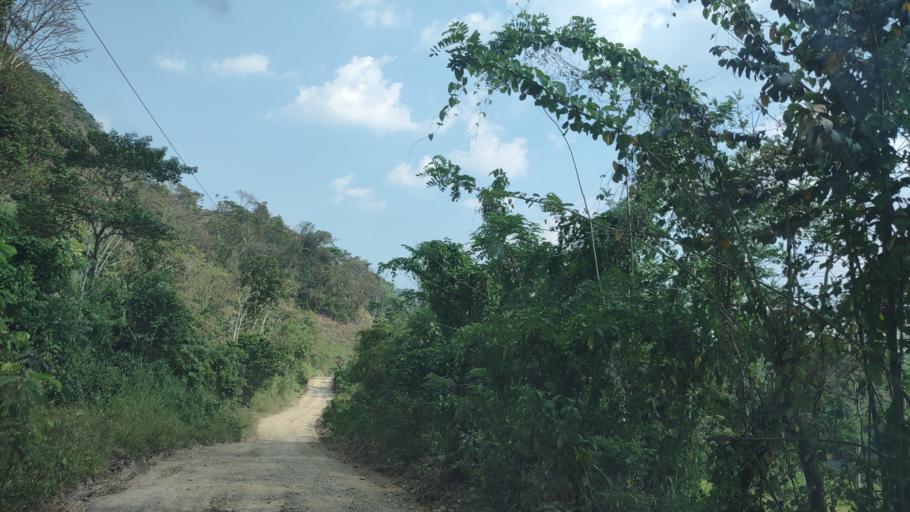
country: MX
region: Chiapas
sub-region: Tecpatan
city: Raudales Malpaso
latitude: 17.3205
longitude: -93.7420
